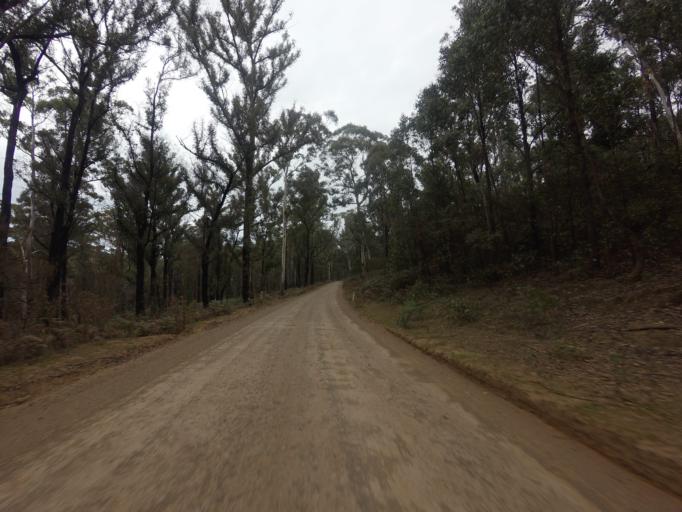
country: AU
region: Tasmania
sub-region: Derwent Valley
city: New Norfolk
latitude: -42.5666
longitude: 146.9752
